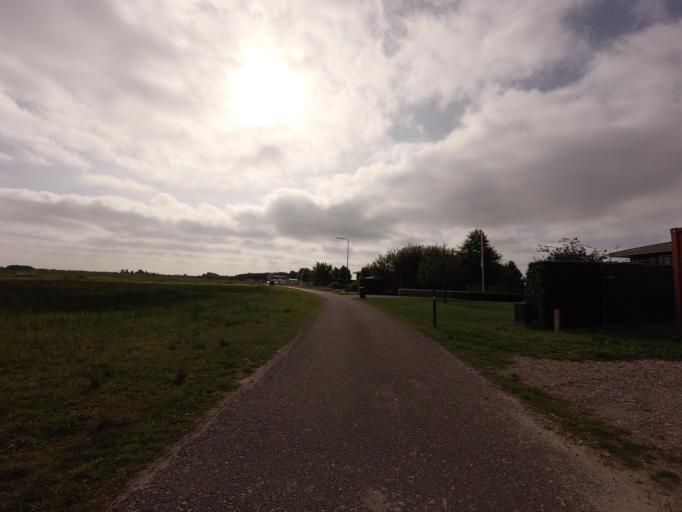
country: NL
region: Overijssel
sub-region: Gemeente Steenwijkerland
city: Steenwijk
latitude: 52.8058
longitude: 6.1421
